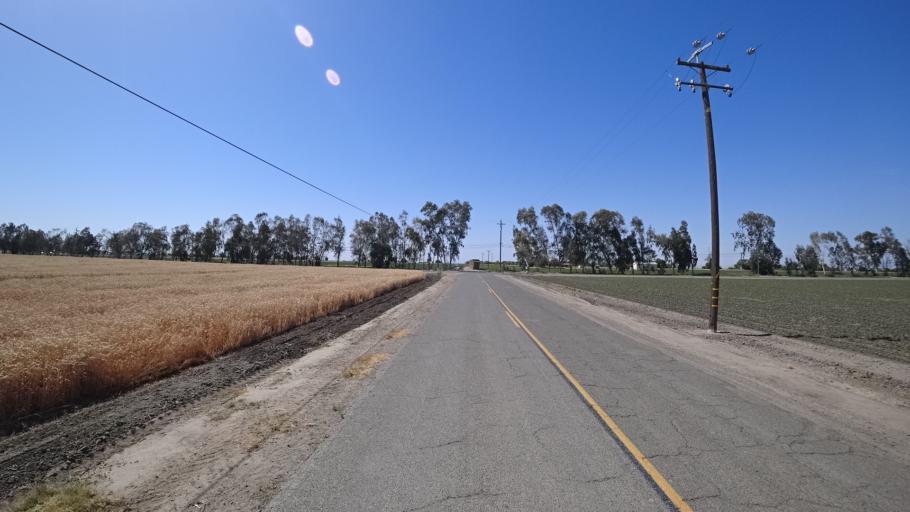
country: US
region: California
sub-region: Kings County
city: Stratford
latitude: 36.1903
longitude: -119.8340
